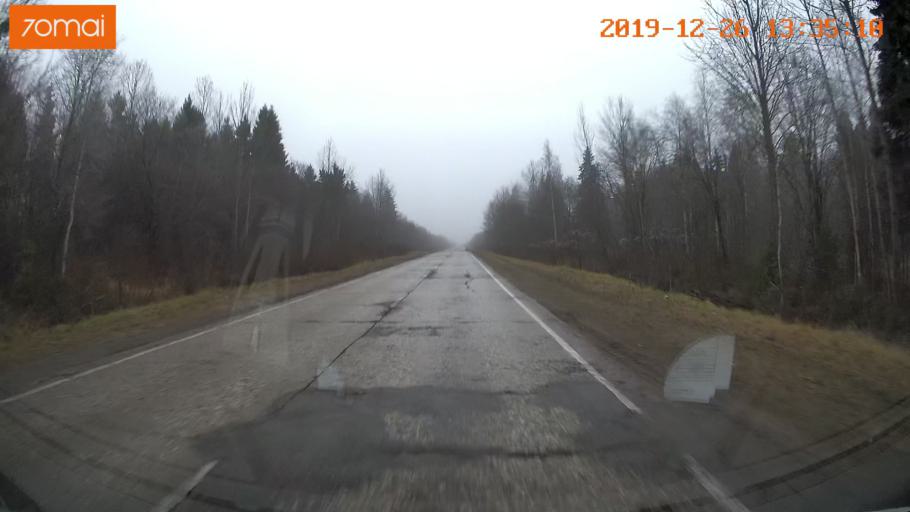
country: RU
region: Vologda
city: Sheksna
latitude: 58.7968
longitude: 38.3357
